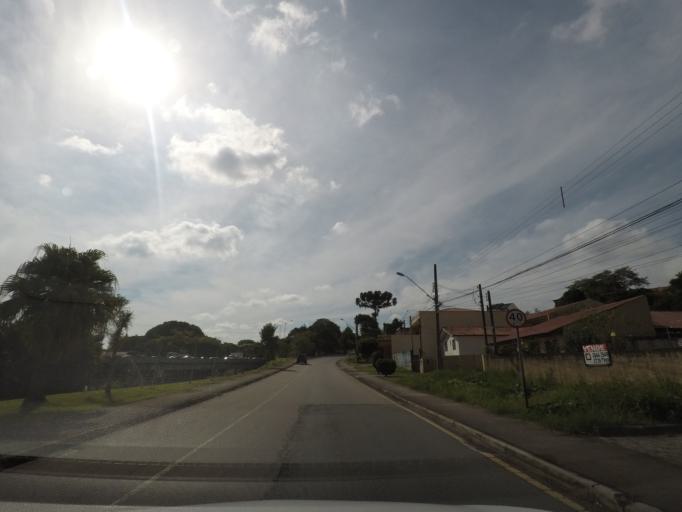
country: BR
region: Parana
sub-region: Curitiba
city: Curitiba
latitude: -25.4579
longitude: -49.2485
